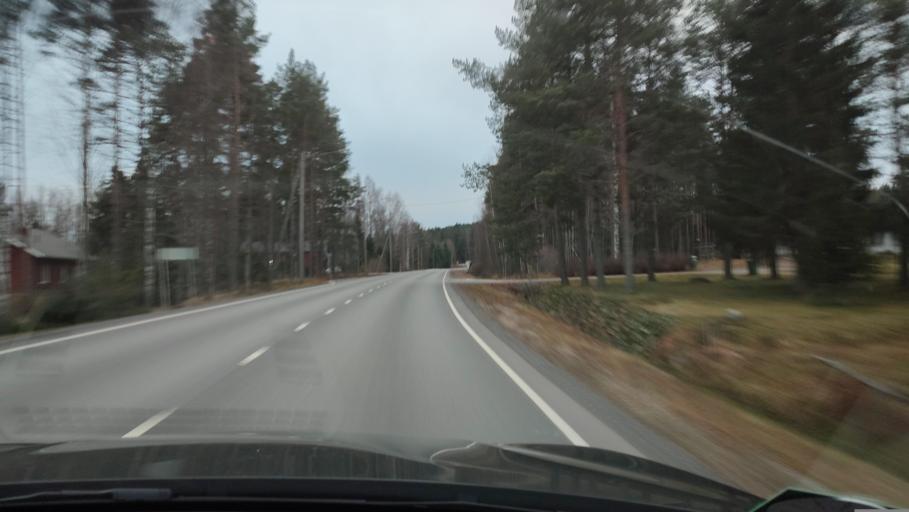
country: FI
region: Southern Ostrobothnia
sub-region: Suupohja
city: Karijoki
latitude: 62.3034
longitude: 21.6906
